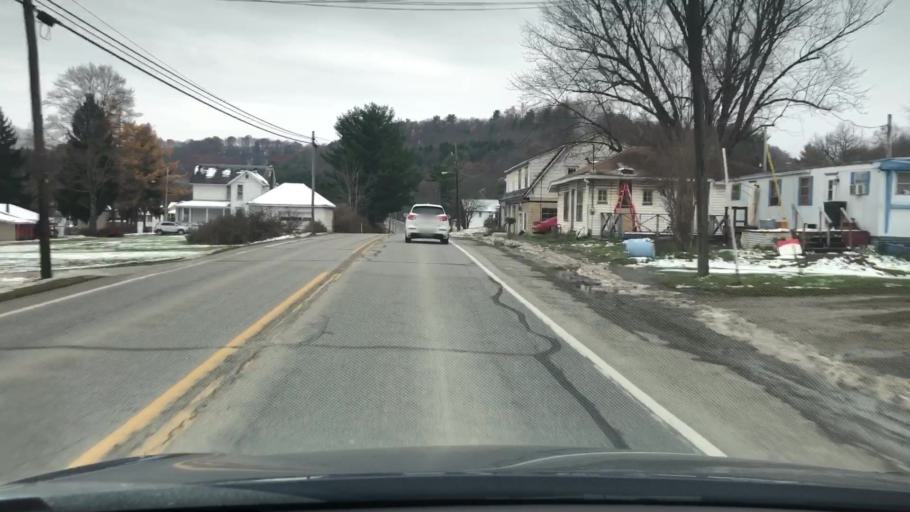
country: US
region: Pennsylvania
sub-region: Jefferson County
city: Brookville
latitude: 41.1184
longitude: -79.1923
